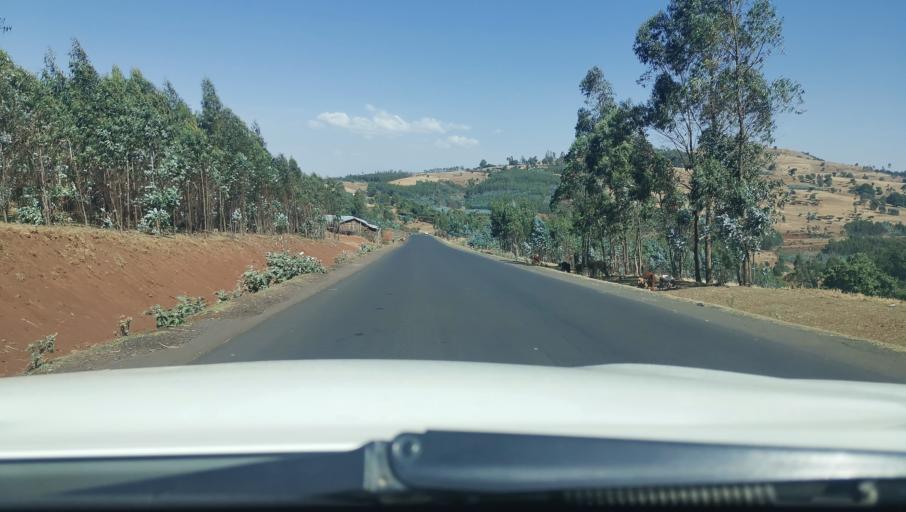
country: ET
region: Oromiya
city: Gedo
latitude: 8.9794
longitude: 37.4678
